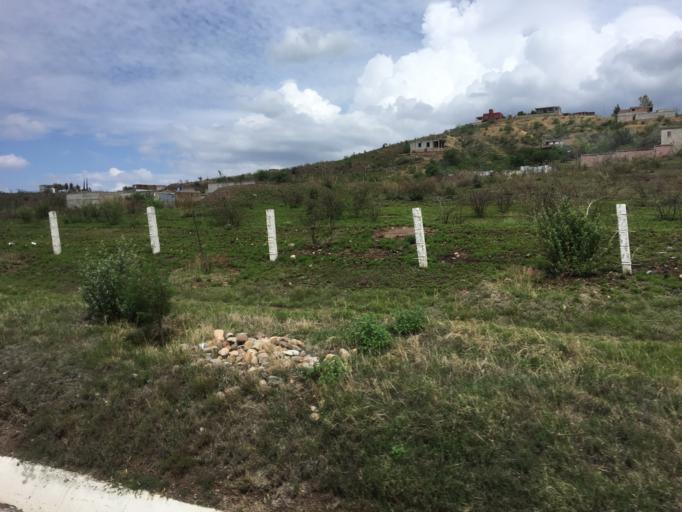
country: MX
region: Guanajuato
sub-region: Guanajuato
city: San Jose de Cervera
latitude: 20.9801
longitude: -101.2918
